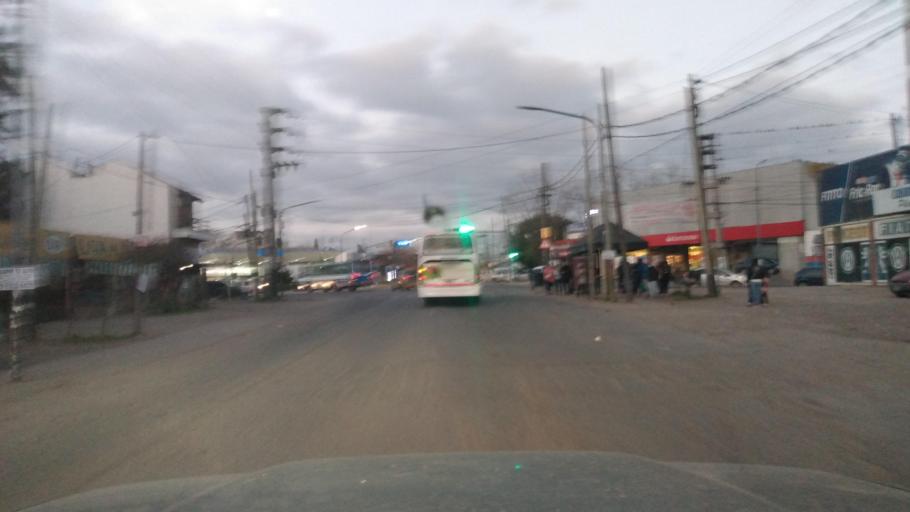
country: AR
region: Buenos Aires
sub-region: Partido de Pilar
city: Pilar
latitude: -34.4544
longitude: -58.9101
